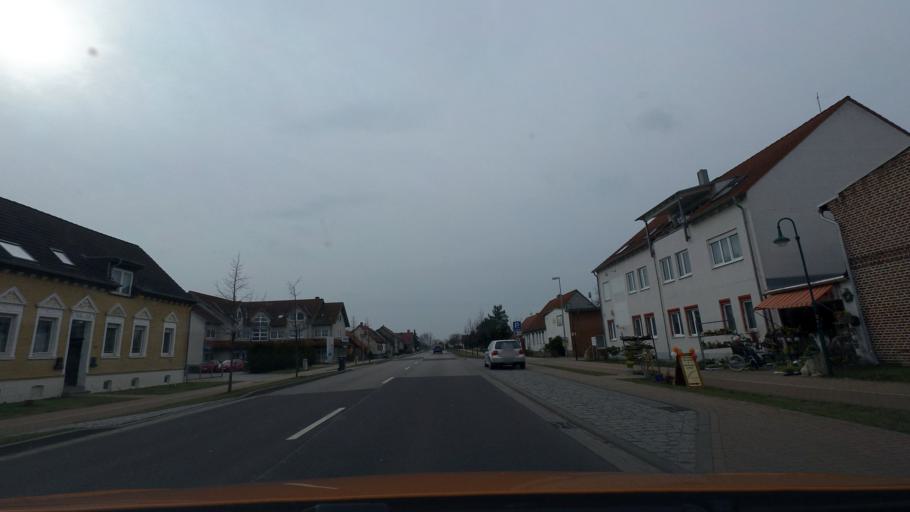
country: DE
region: Saxony-Anhalt
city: Gerwisch
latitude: 52.1728
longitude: 11.7459
